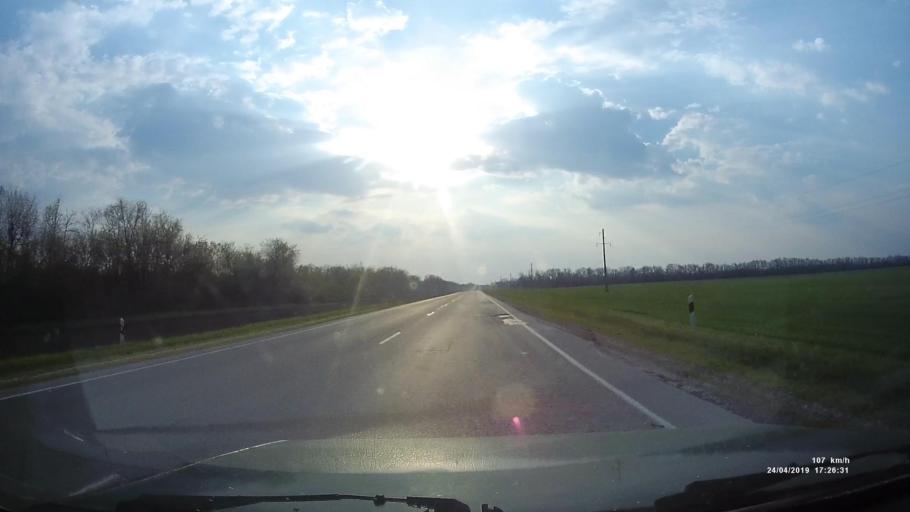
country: RU
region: Rostov
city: Gigant
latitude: 46.5264
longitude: 41.2192
